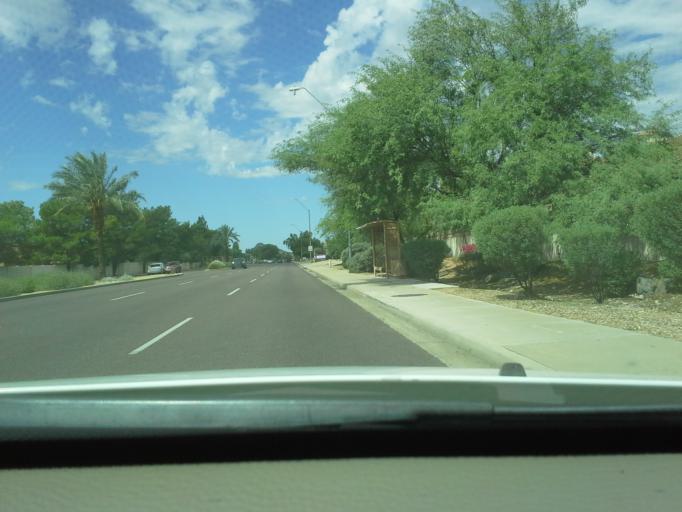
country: US
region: Arizona
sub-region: Maricopa County
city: Paradise Valley
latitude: 33.6262
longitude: -111.9728
